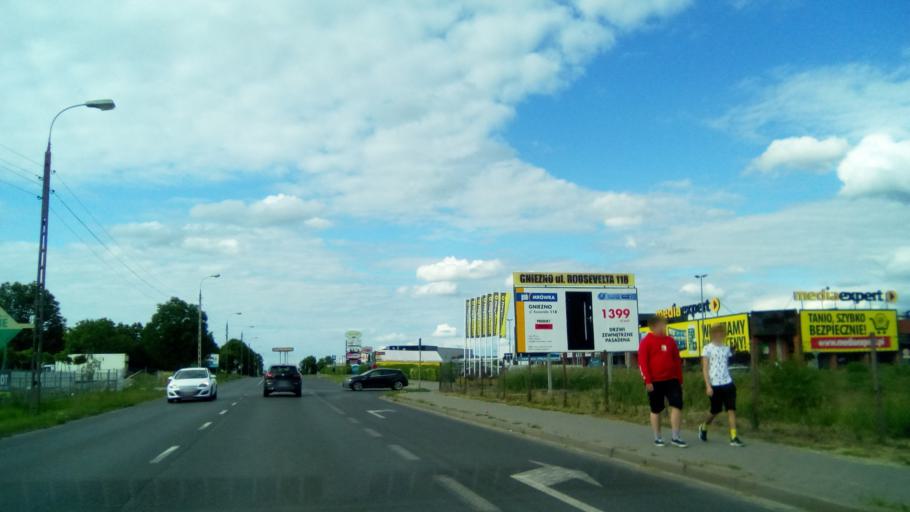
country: PL
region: Greater Poland Voivodeship
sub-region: Powiat gnieznienski
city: Gniezno
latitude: 52.5583
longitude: 17.6080
